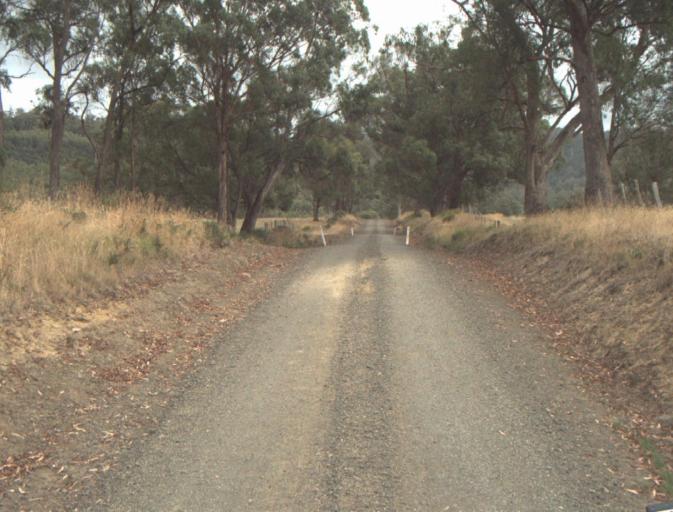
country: AU
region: Tasmania
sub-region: Dorset
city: Scottsdale
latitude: -41.4664
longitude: 147.5738
